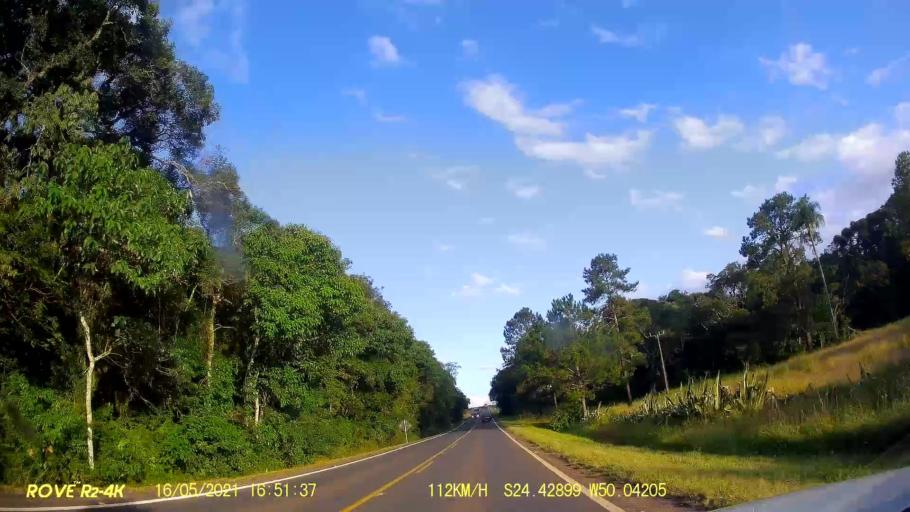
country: BR
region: Parana
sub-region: Pirai Do Sul
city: Pirai do Sul
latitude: -24.4291
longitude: -50.0419
